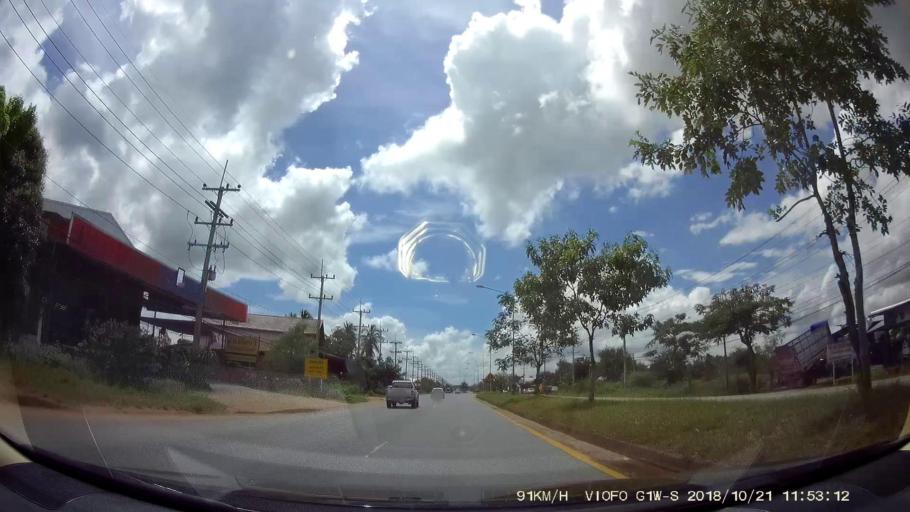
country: TH
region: Chaiyaphum
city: Chatturat
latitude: 15.5989
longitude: 101.9073
